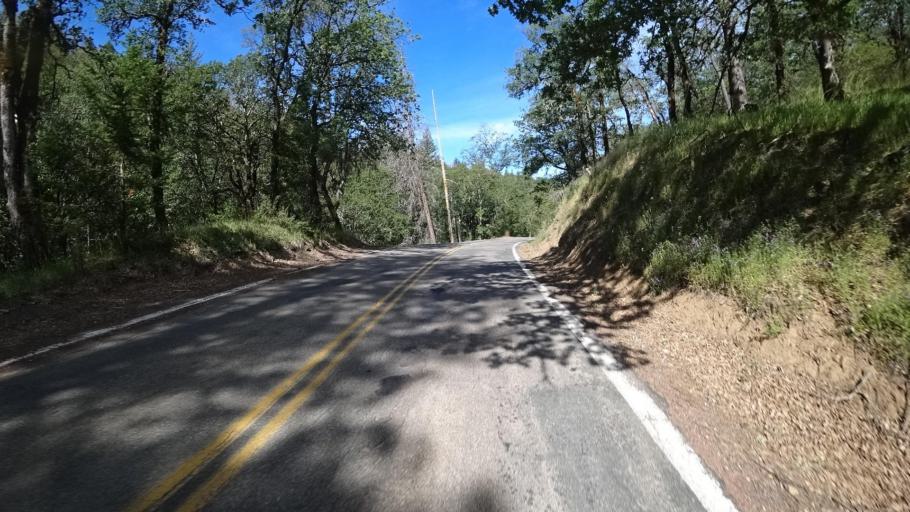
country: US
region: California
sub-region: Lake County
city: Cobb
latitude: 38.8555
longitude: -122.7360
